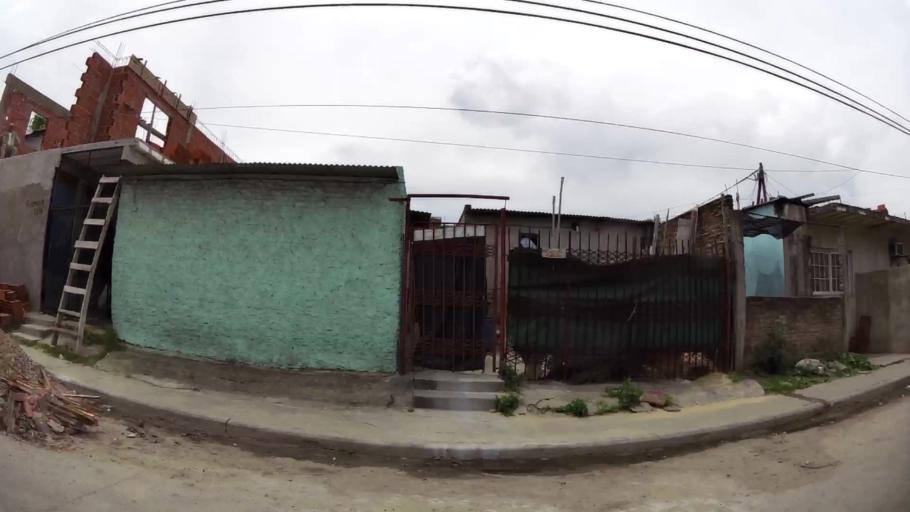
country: AR
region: Buenos Aires
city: San Justo
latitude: -34.6729
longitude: -58.5430
